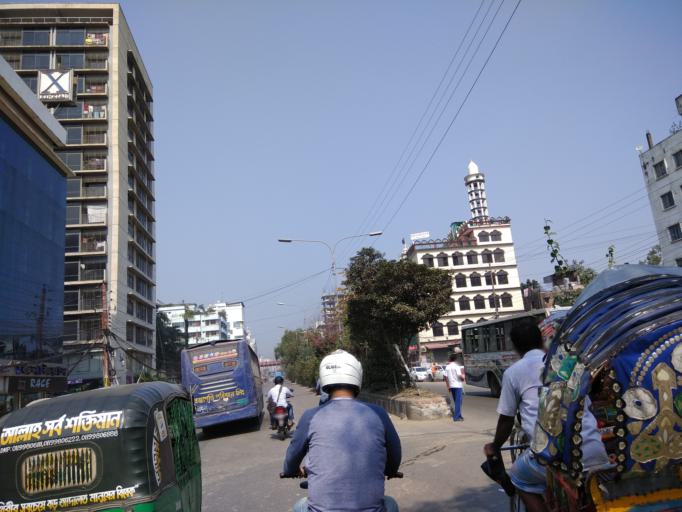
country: BD
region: Dhaka
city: Azimpur
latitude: 23.8126
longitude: 90.3670
